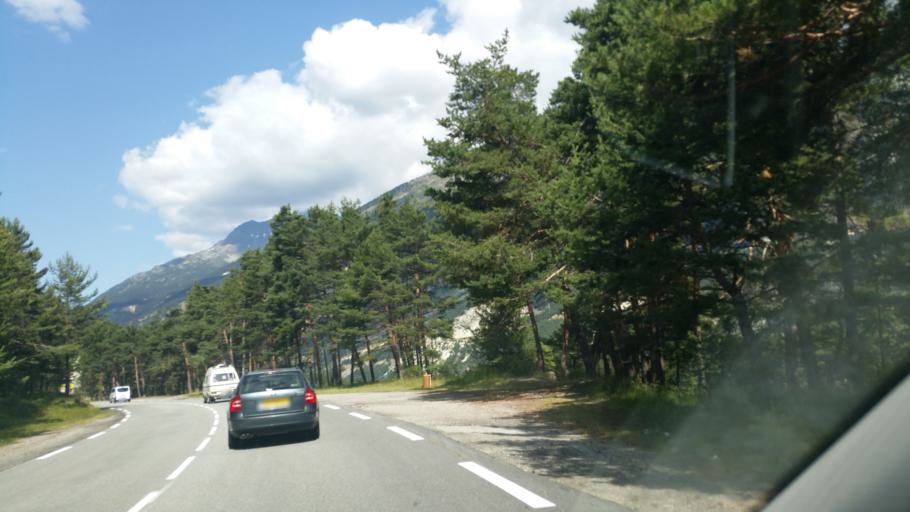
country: FR
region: Rhone-Alpes
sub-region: Departement de la Savoie
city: Modane
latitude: 45.2088
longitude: 6.7319
